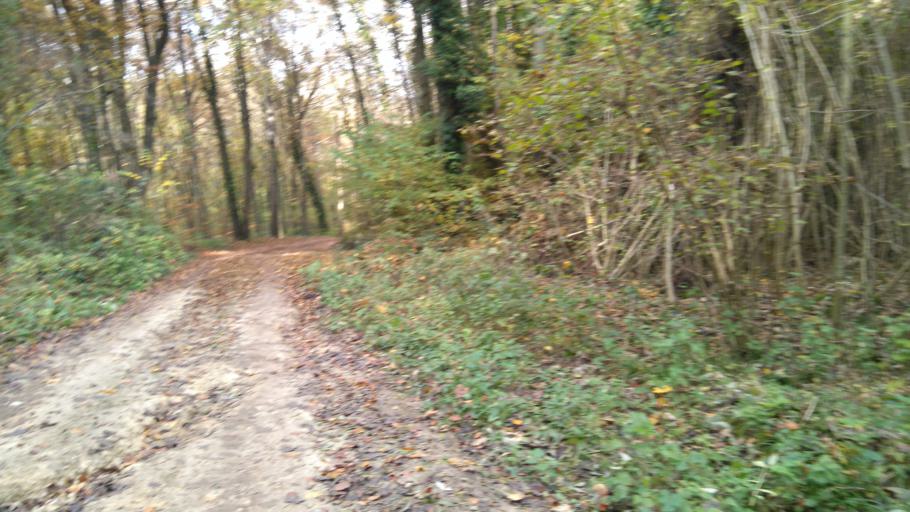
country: FR
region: Picardie
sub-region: Departement de l'Oise
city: Balagny-sur-Therain
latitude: 49.2829
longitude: 2.3460
